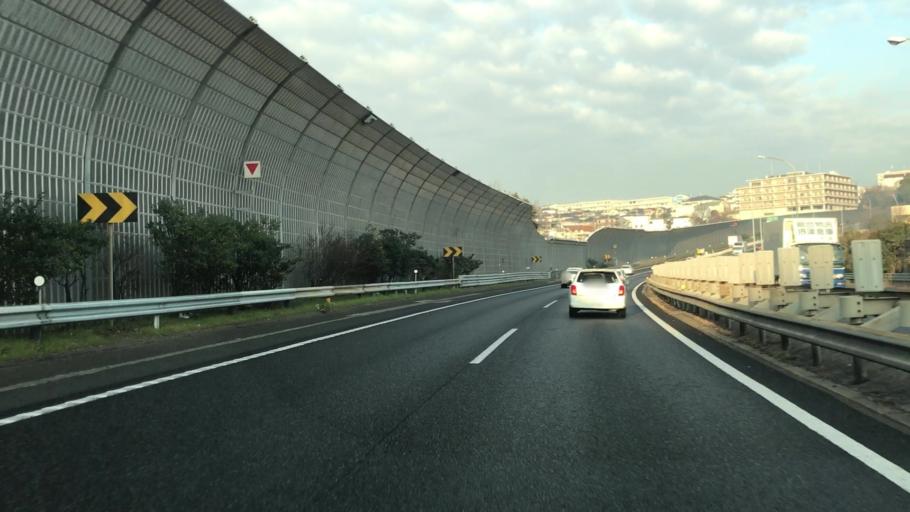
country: JP
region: Hyogo
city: Akashi
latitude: 34.6518
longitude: 135.0392
